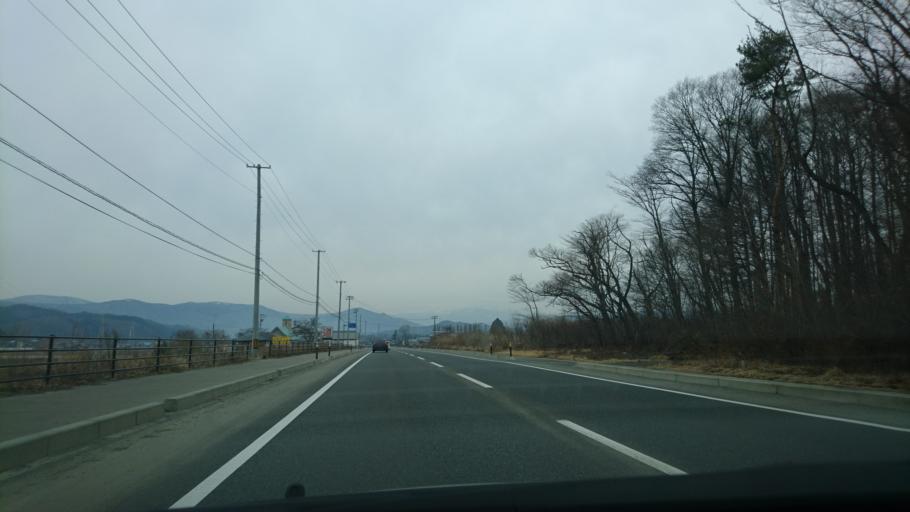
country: JP
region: Iwate
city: Tono
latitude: 39.3038
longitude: 141.5755
